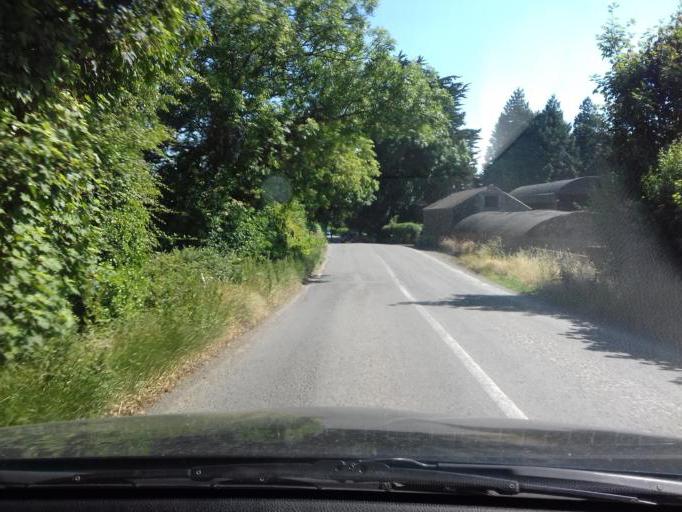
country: IE
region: Leinster
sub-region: An Mhi
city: Stamullin
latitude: 53.5707
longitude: -6.2812
